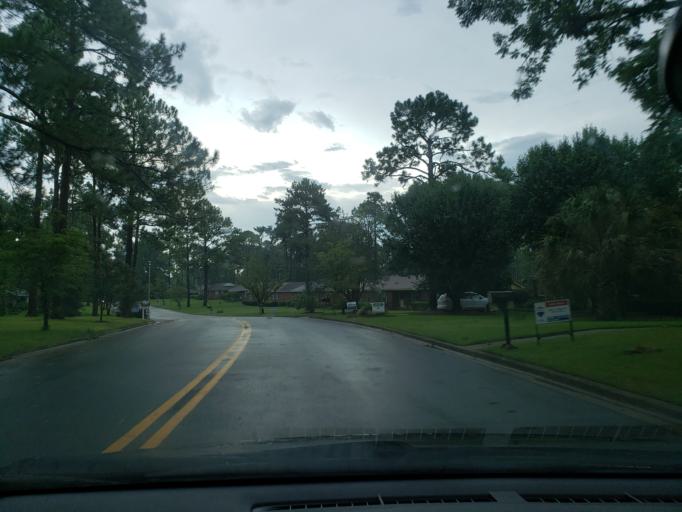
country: US
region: Georgia
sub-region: Dougherty County
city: Albany
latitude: 31.5966
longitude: -84.2056
